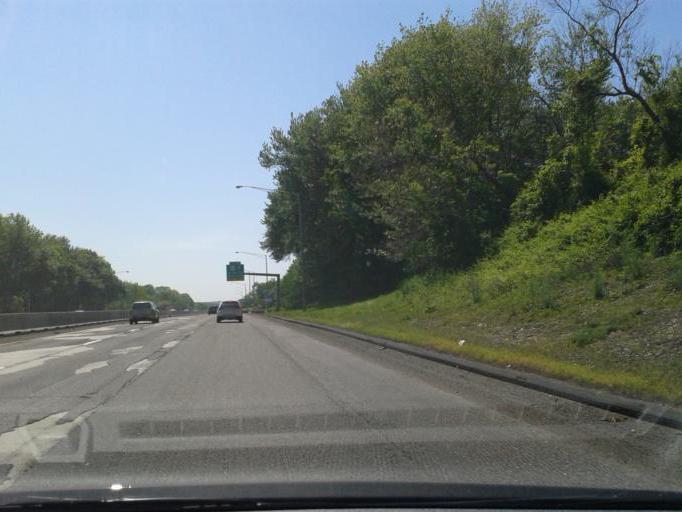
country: US
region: Connecticut
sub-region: New London County
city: Central Waterford
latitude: 41.3713
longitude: -72.1285
